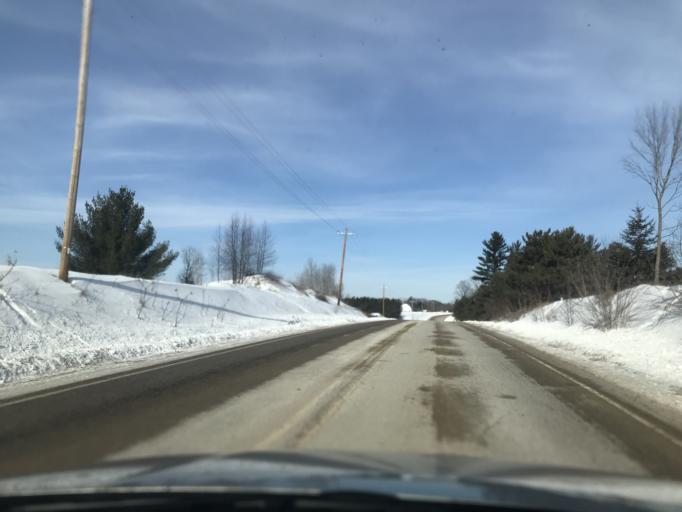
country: US
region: Wisconsin
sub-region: Oconto County
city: Oconto Falls
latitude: 45.1432
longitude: -88.1771
